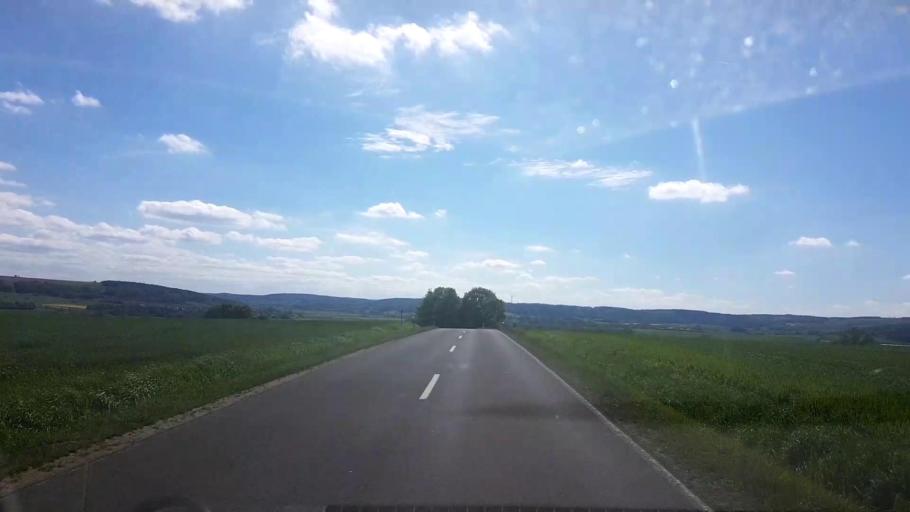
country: DE
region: Bavaria
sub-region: Regierungsbezirk Unterfranken
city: Untermerzbach
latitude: 50.1476
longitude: 10.8911
